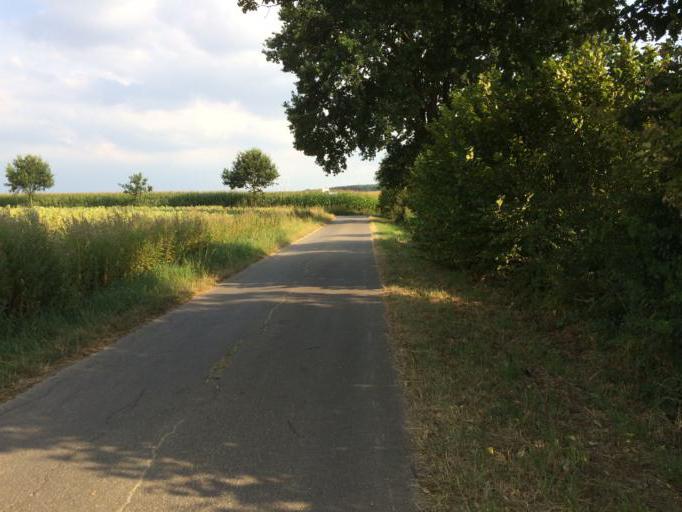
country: DE
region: North Rhine-Westphalia
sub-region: Regierungsbezirk Detmold
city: Nieheim
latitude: 51.8200
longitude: 9.1498
